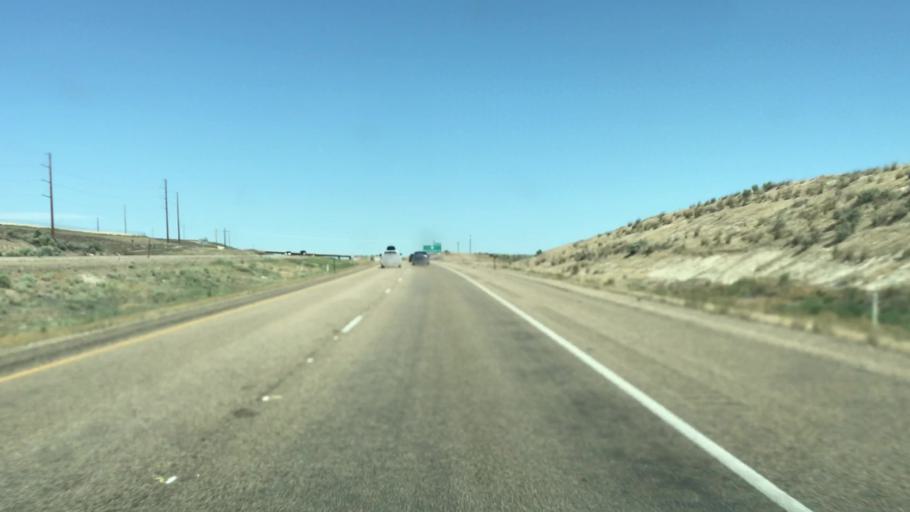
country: US
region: Idaho
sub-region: Payette County
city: New Plymouth
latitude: 43.9019
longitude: -116.8102
